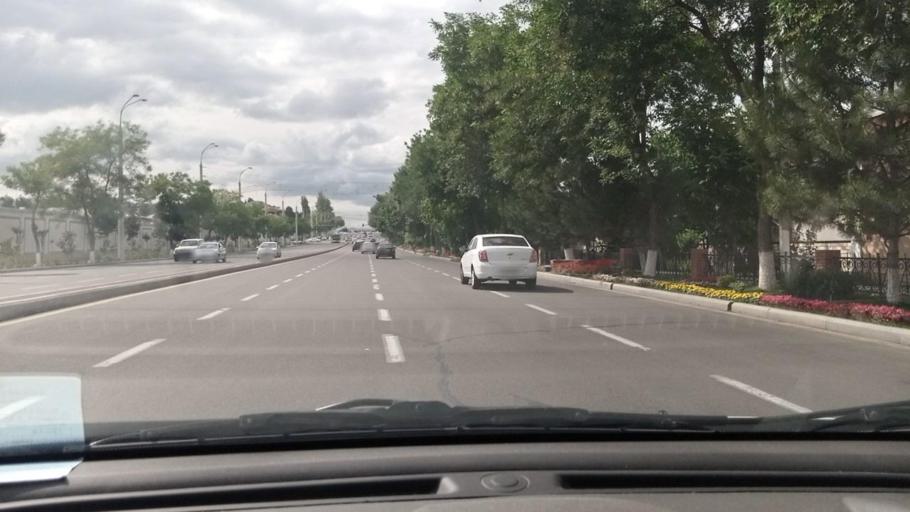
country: UZ
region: Toshkent
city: Salor
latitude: 41.3275
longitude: 69.3574
